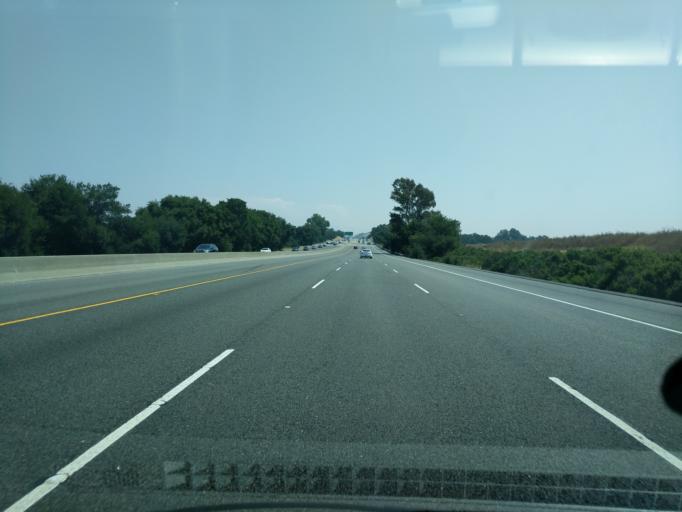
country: US
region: California
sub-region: Alameda County
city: Pleasanton
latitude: 37.6505
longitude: -121.8951
